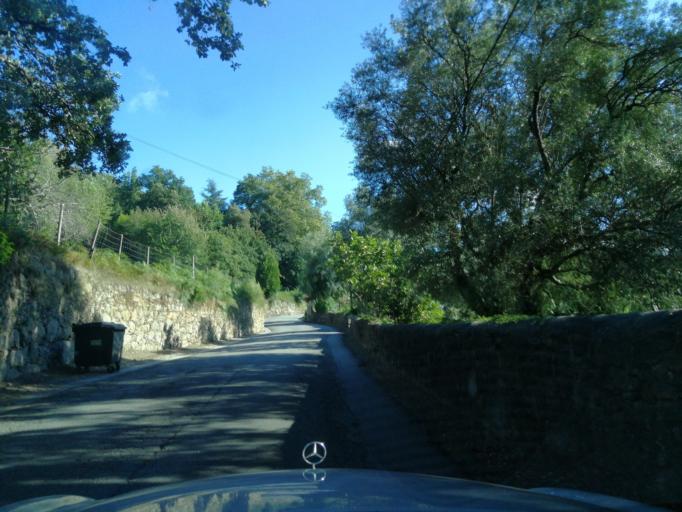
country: PT
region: Braga
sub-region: Braga
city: Adaufe
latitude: 41.5563
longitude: -8.3813
